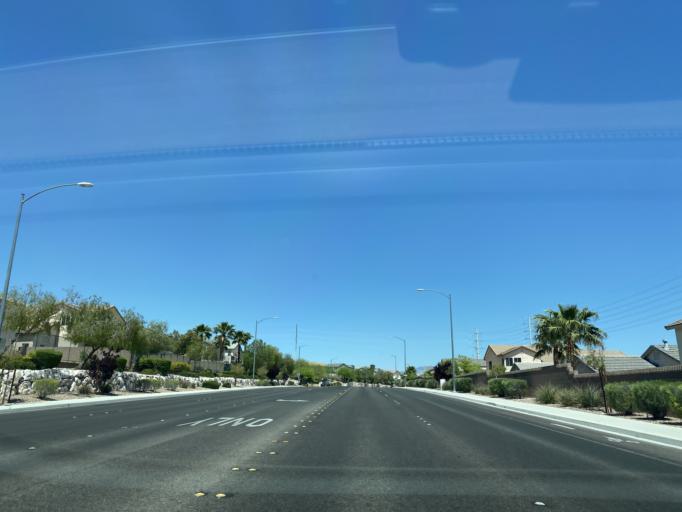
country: US
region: Nevada
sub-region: Clark County
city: Summerlin South
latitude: 36.2363
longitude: -115.3306
